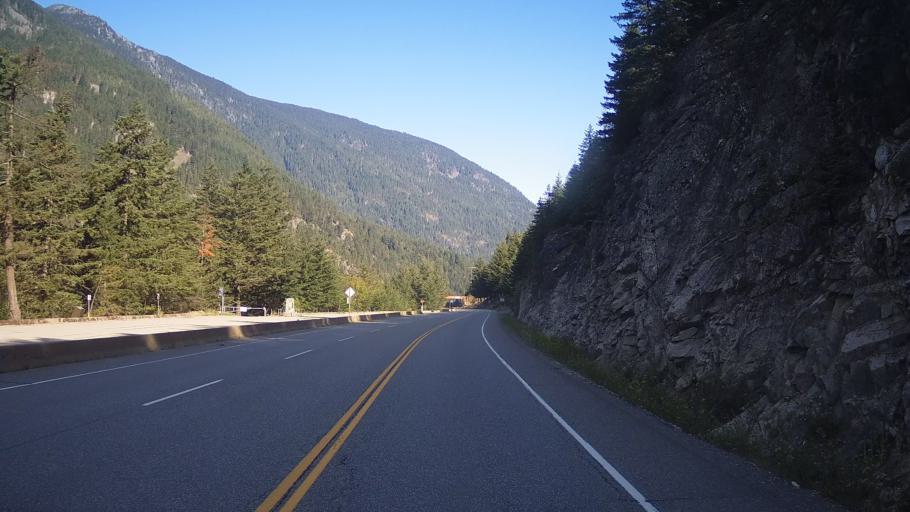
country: CA
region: British Columbia
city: Hope
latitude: 49.7773
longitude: -121.4415
